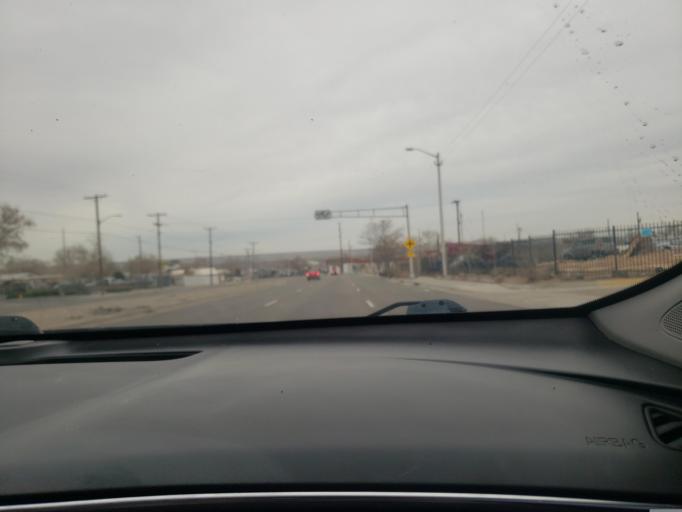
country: US
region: New Mexico
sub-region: Bernalillo County
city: Albuquerque
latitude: 35.0605
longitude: -106.6412
